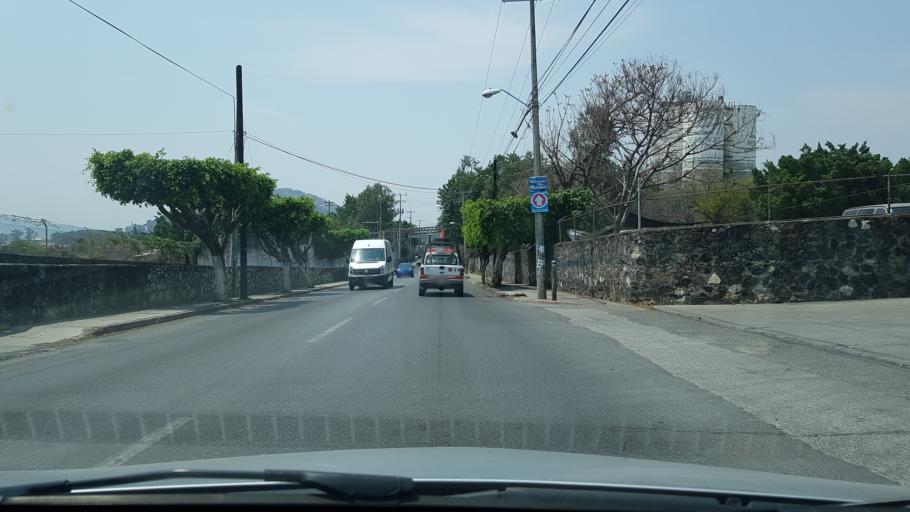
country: MX
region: Morelos
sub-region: Jiutepec
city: Jiutepec
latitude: 18.8926
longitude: -99.1718
